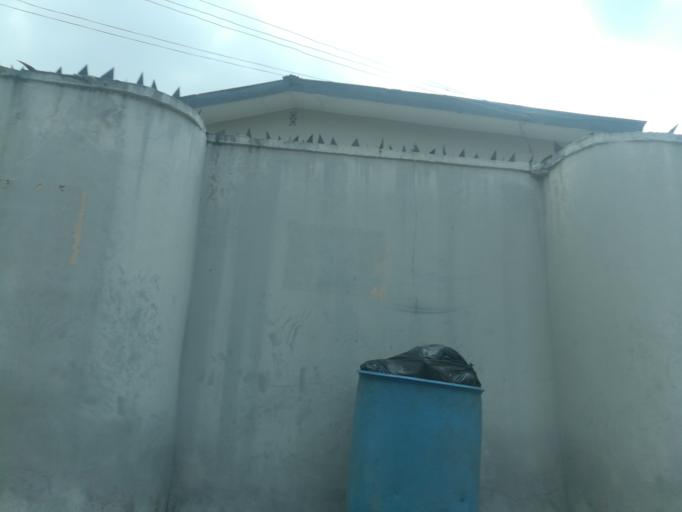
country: NG
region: Oyo
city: Ibadan
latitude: 7.3606
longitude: 3.8663
